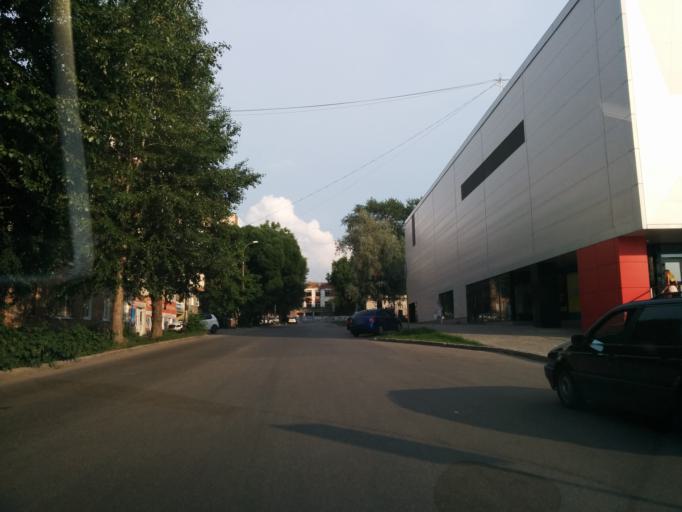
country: RU
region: Perm
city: Perm
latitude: 58.0272
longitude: 56.2950
